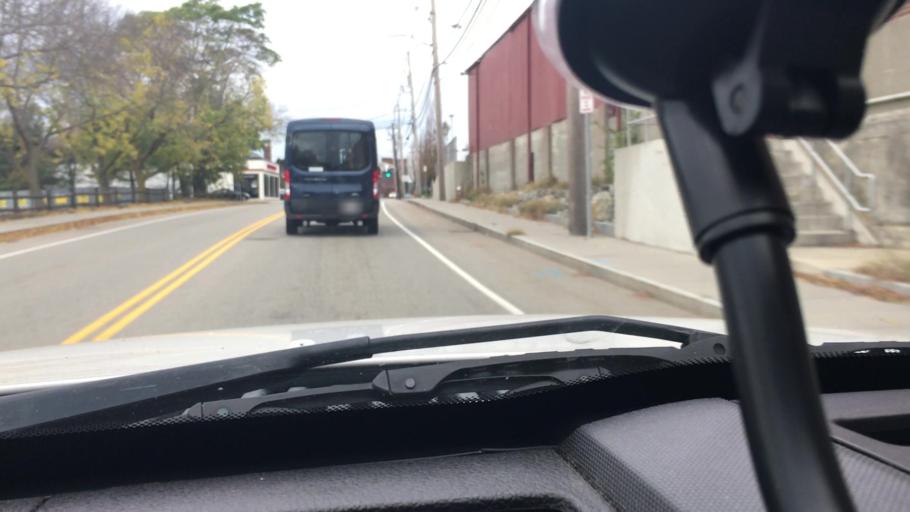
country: US
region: Massachusetts
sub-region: Middlesex County
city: Watertown
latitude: 42.3671
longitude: -71.2024
